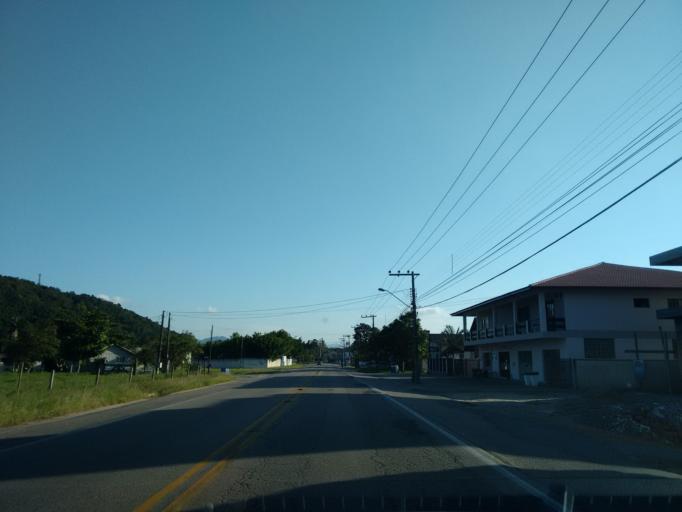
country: BR
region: Santa Catarina
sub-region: Gaspar
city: Gaspar
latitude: -26.9150
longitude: -48.9437
